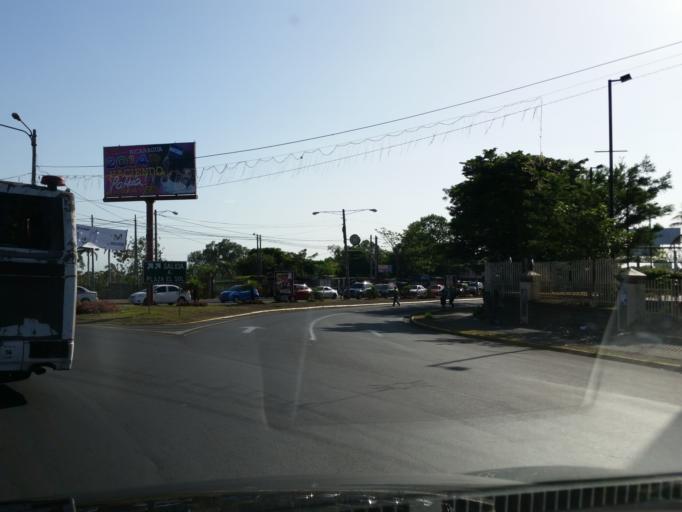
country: NI
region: Managua
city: Managua
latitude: 12.1290
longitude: -86.2660
